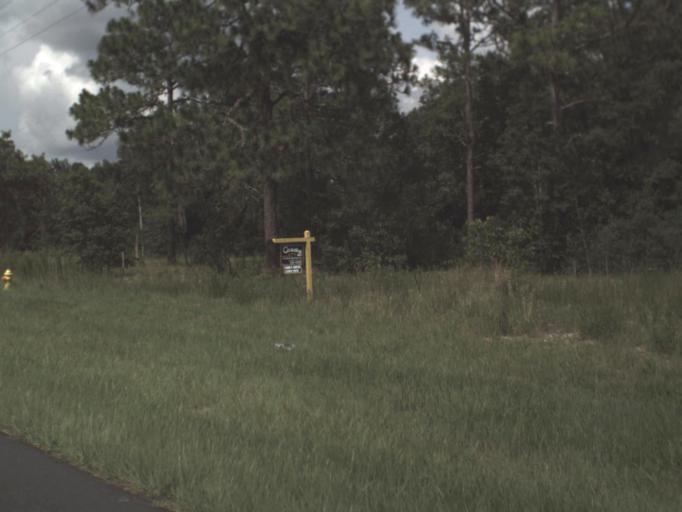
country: US
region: Florida
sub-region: Citrus County
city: Floral City
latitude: 28.7366
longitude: -82.3020
